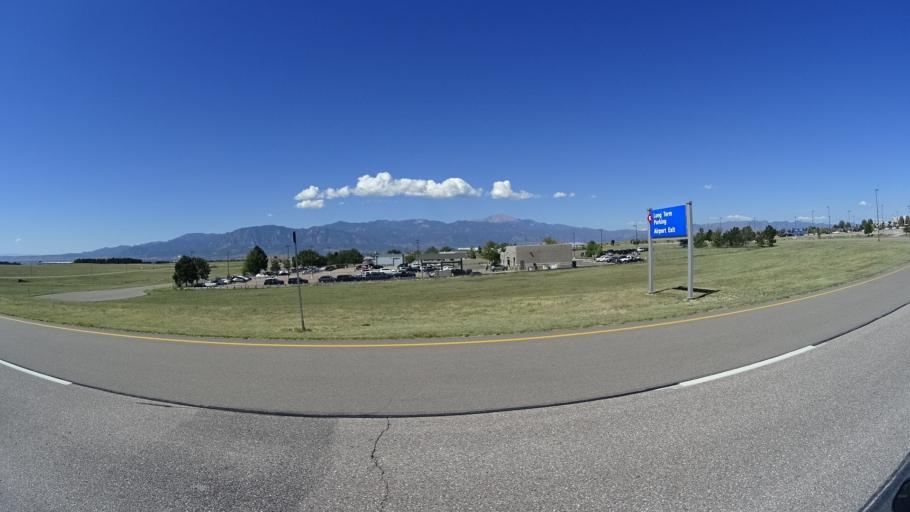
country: US
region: Colorado
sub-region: El Paso County
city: Security-Widefield
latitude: 38.7910
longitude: -104.6972
